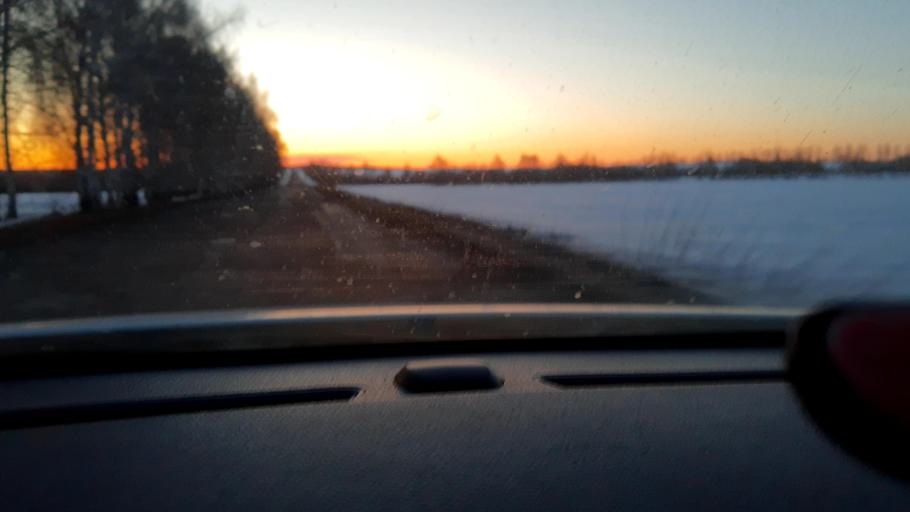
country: RU
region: Bashkortostan
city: Avdon
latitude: 54.3878
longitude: 55.7484
